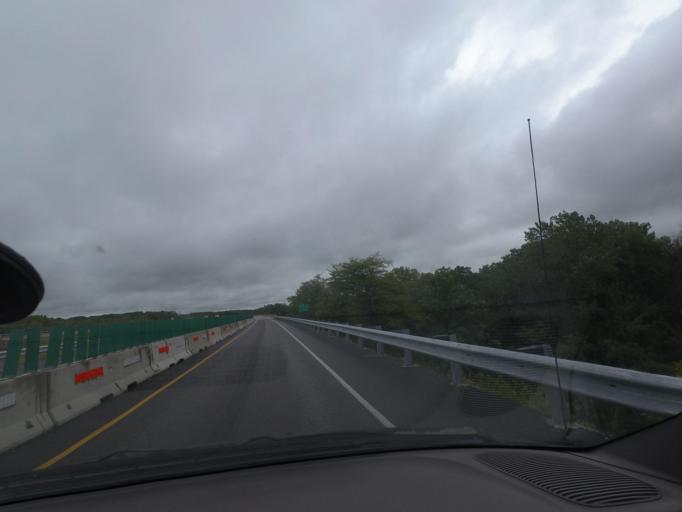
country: US
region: Illinois
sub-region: Piatt County
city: Cerro Gordo
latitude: 39.9788
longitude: -88.7959
